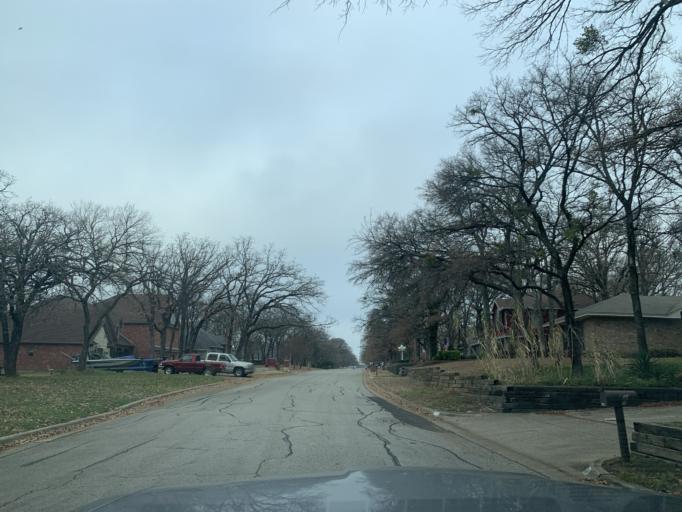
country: US
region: Texas
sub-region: Tarrant County
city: Bedford
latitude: 32.8336
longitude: -97.1438
